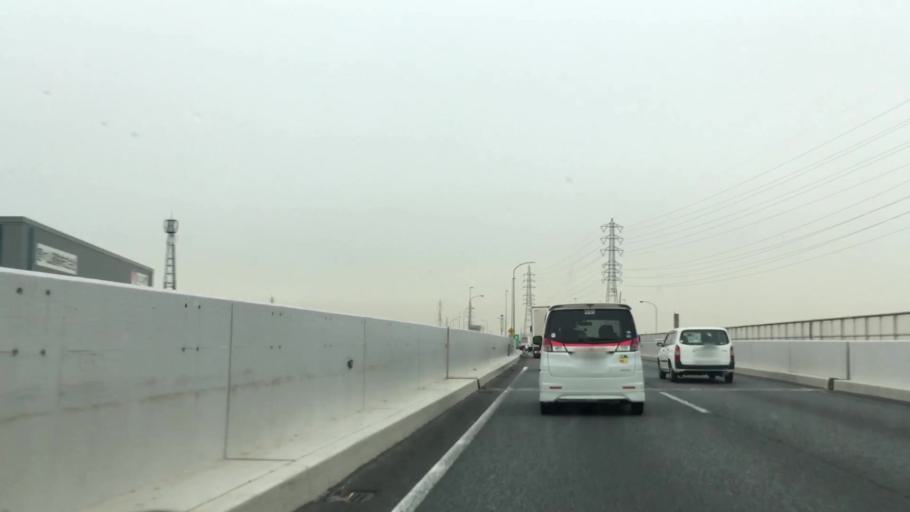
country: JP
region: Aichi
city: Chiryu
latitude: 35.0028
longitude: 137.0278
